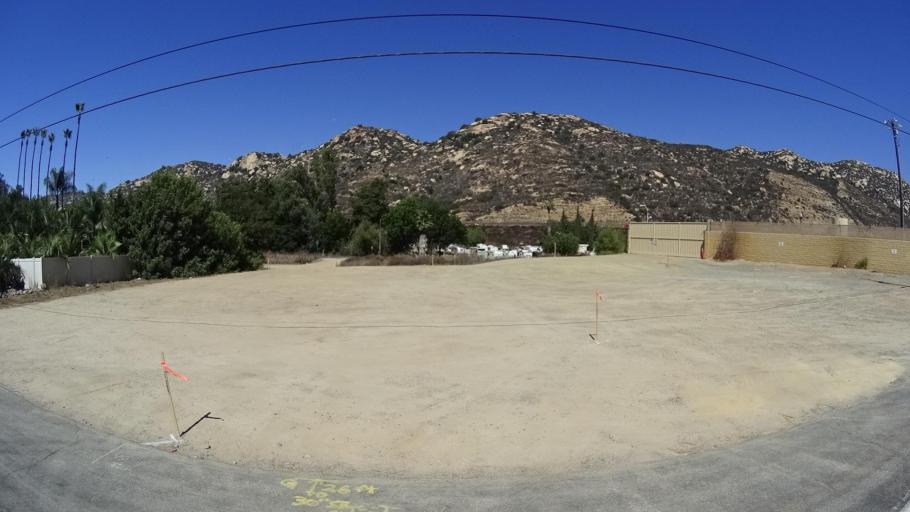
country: US
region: California
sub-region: San Diego County
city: Rainbow
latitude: 33.4321
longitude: -117.1402
